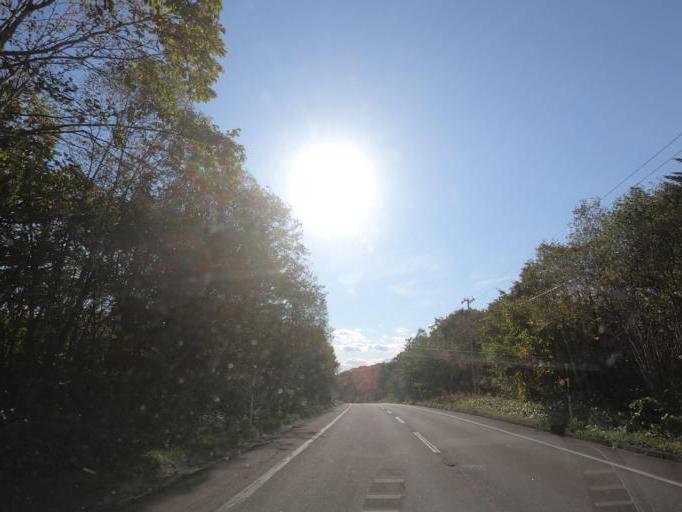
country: JP
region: Hokkaido
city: Obihiro
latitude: 42.6112
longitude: 143.4621
